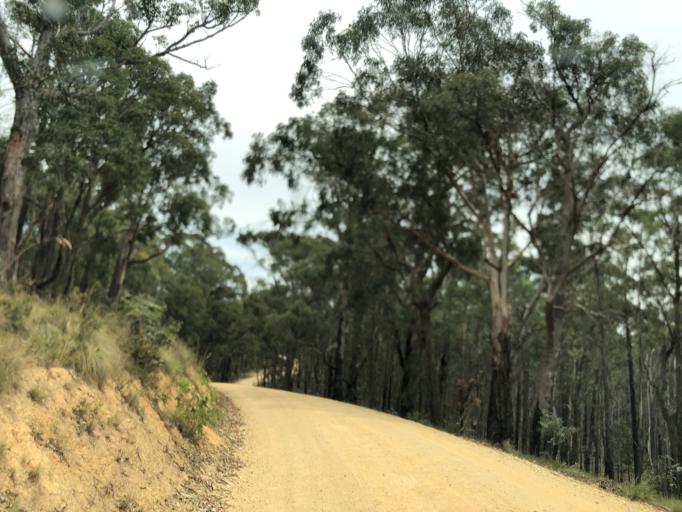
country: AU
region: Victoria
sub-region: Moorabool
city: Bacchus Marsh
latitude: -37.5003
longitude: 144.3338
